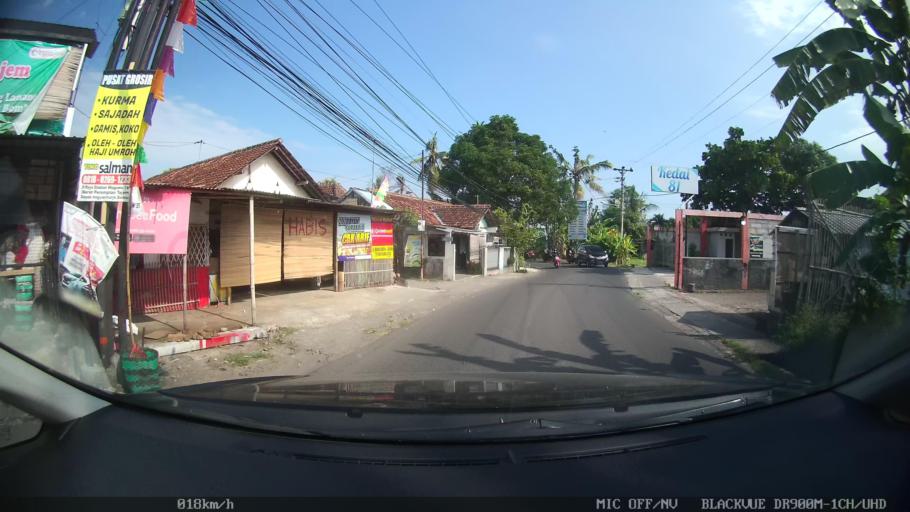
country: ID
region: Daerah Istimewa Yogyakarta
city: Depok
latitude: -7.7517
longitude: 110.4354
